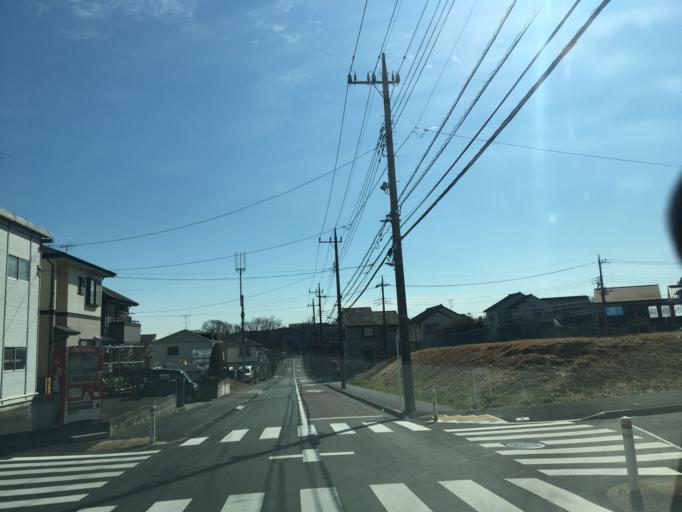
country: JP
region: Tokyo
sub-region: Machida-shi
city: Machida
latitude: 35.5865
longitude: 139.4145
